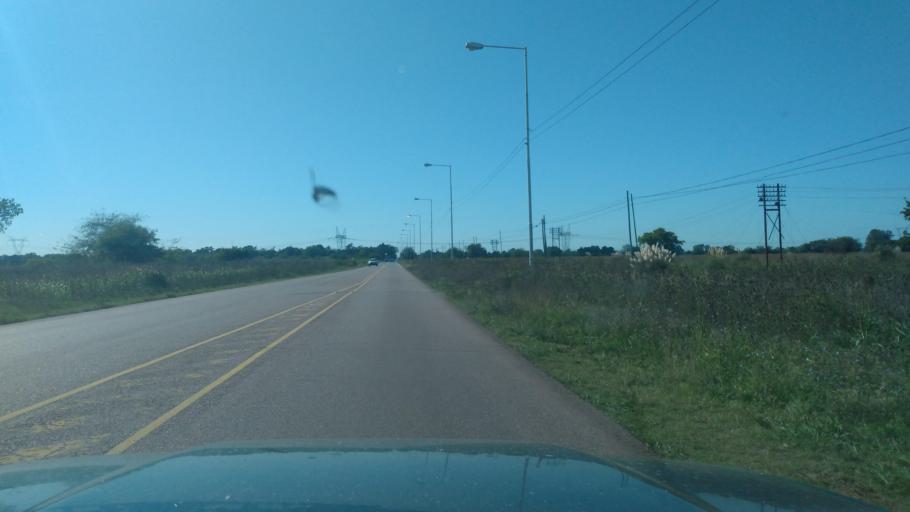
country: AR
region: Buenos Aires
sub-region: Partido de Lujan
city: Lujan
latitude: -34.5901
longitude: -59.0316
